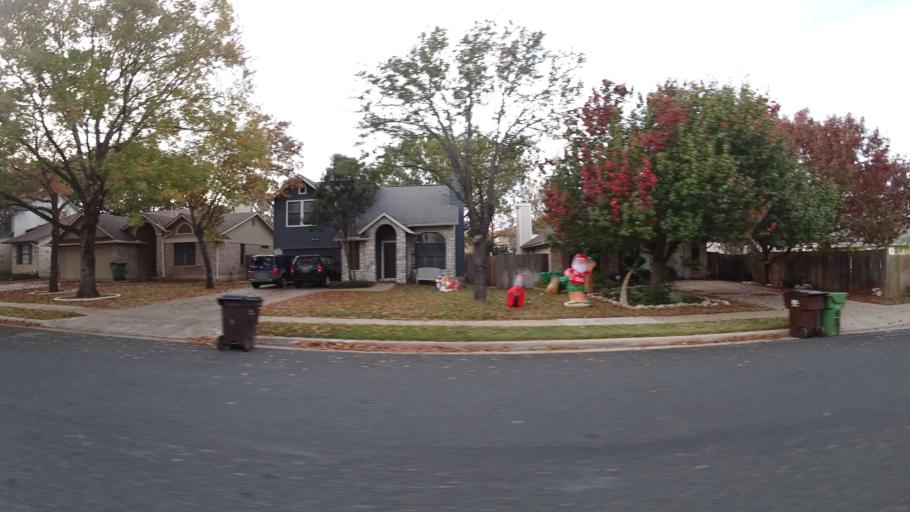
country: US
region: Texas
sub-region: Williamson County
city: Brushy Creek
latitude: 30.5152
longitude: -97.7235
